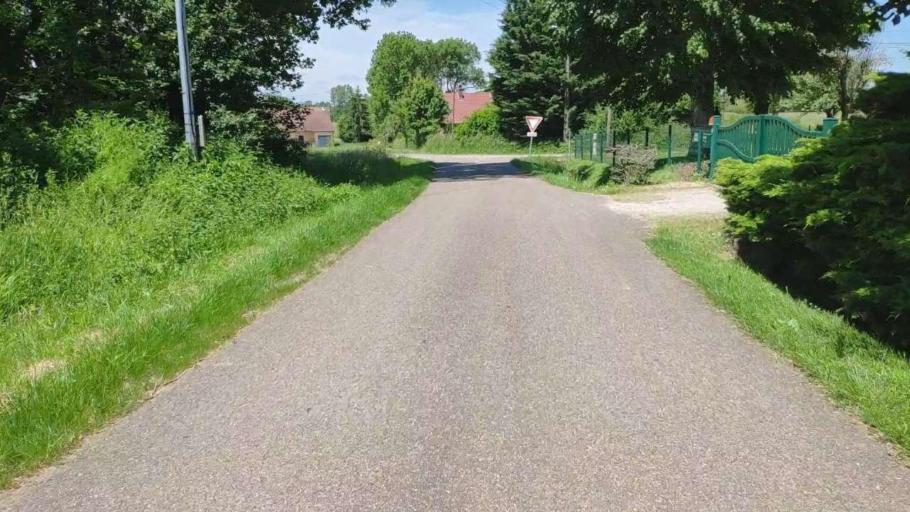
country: FR
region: Franche-Comte
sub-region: Departement du Jura
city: Bletterans
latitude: 46.8044
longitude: 5.3821
